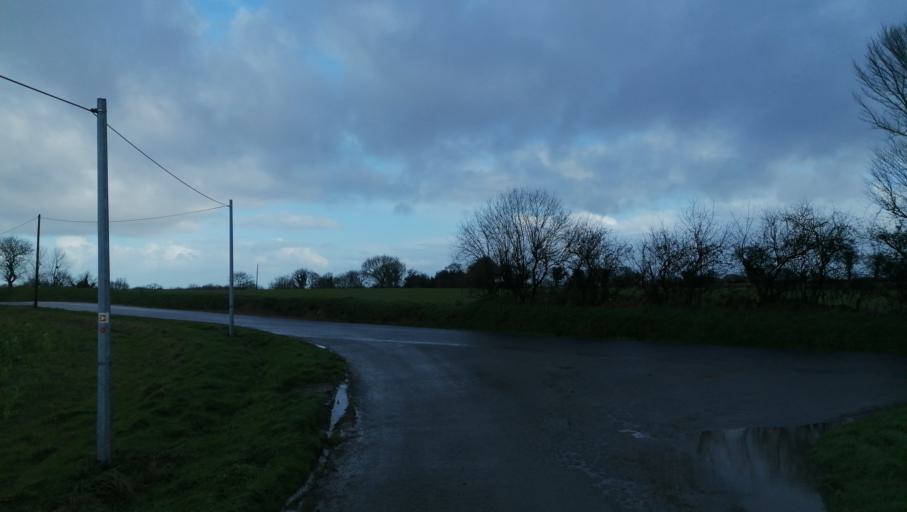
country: FR
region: Brittany
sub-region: Departement des Cotes-d'Armor
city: Lanrodec
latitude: 48.4904
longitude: -3.0022
